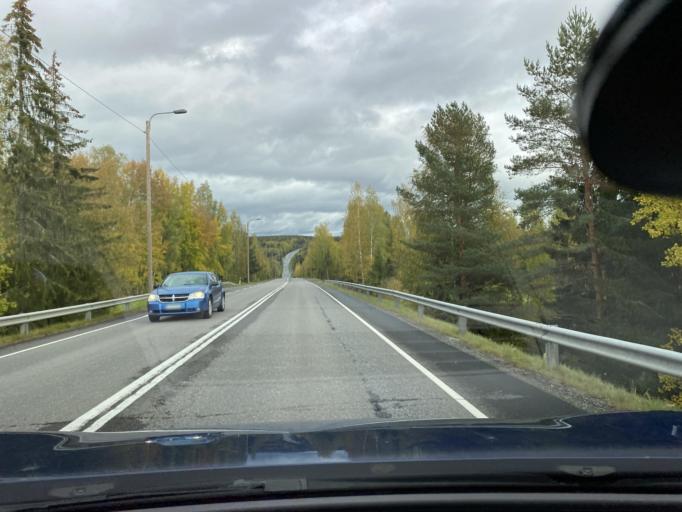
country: FI
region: Pirkanmaa
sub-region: Tampere
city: Haemeenkyroe
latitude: 61.5004
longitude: 23.3179
